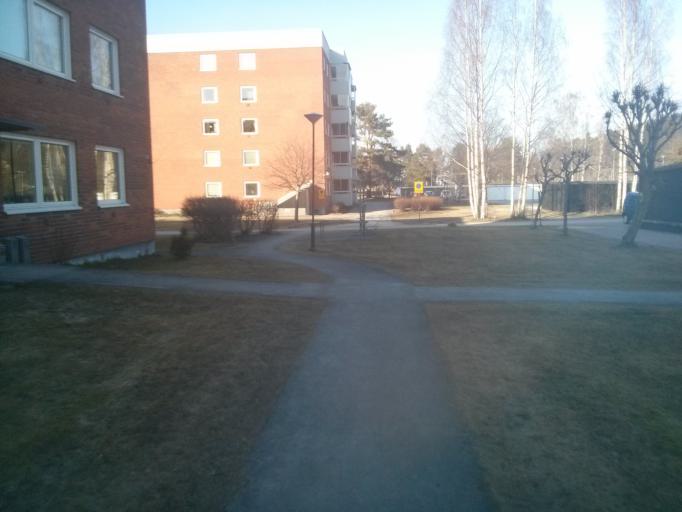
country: SE
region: Vaesternorrland
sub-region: Sundsvalls Kommun
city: Skottsund
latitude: 62.2980
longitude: 17.3828
